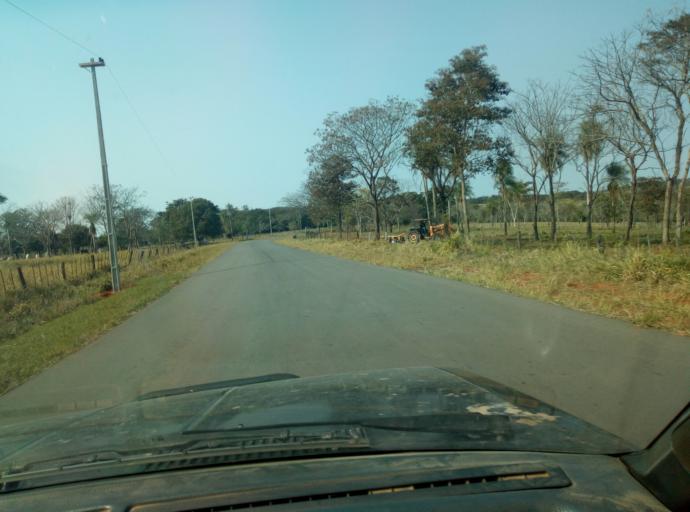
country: PY
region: Caaguazu
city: Carayao
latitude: -25.1935
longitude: -56.3105
